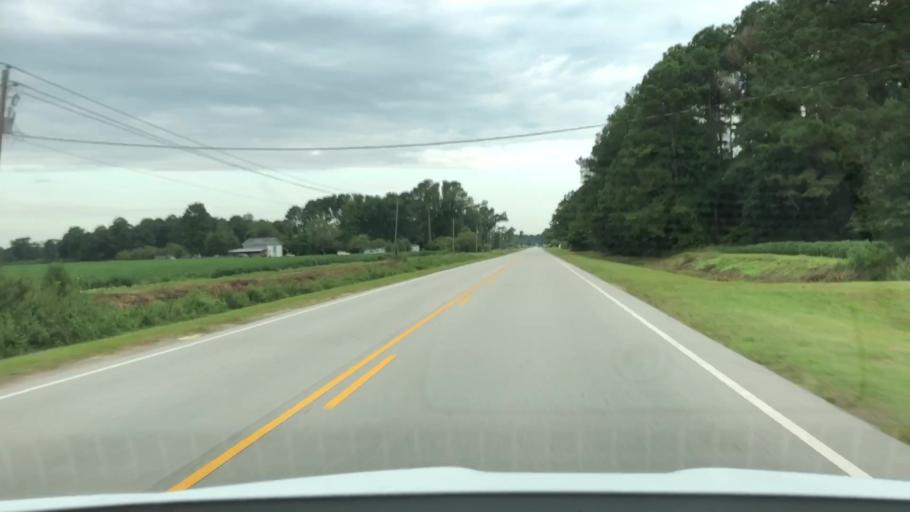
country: US
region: North Carolina
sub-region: Jones County
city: Trenton
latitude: 35.0335
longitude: -77.3221
